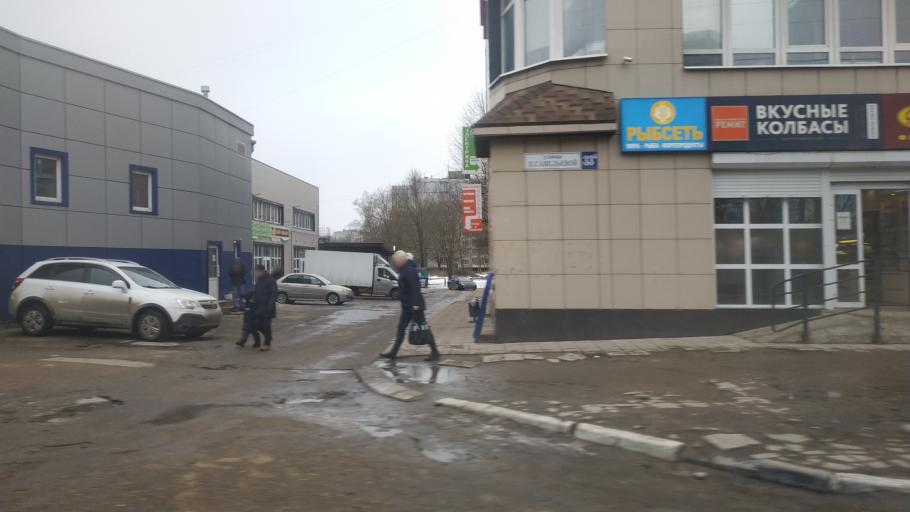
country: RU
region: Tverskaya
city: Tver
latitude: 56.8844
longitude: 35.8399
